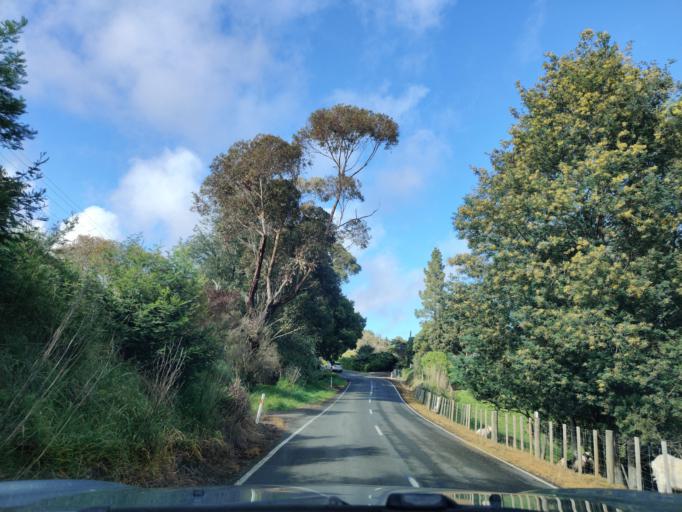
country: NZ
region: Hawke's Bay
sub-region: Hastings District
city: Hastings
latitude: -39.6789
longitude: 176.8964
